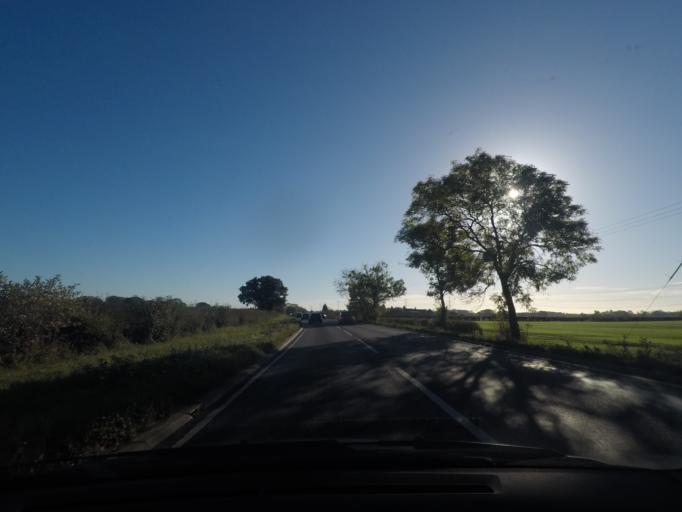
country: GB
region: England
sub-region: East Riding of Yorkshire
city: Wilberfoss
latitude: 53.9519
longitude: -0.9142
